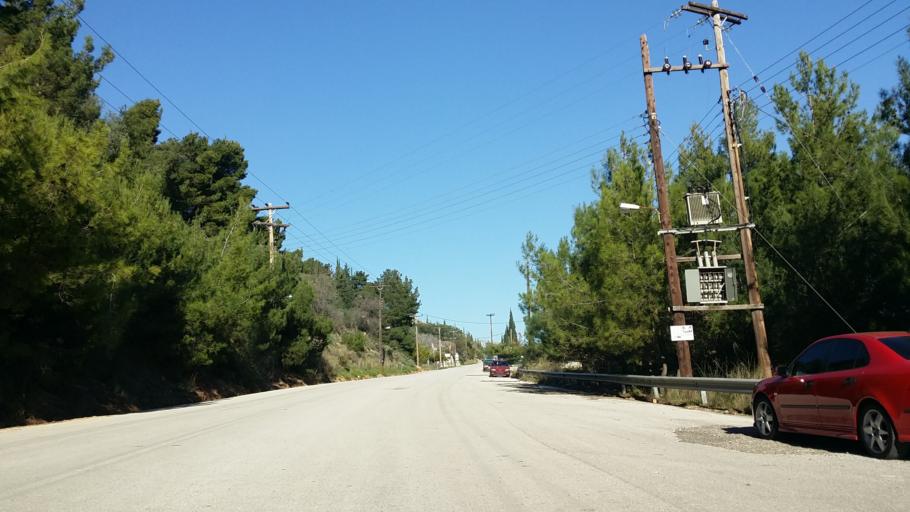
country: GR
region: West Greece
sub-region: Nomos Aitolias kai Akarnanias
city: Astakos
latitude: 38.5344
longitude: 21.0739
